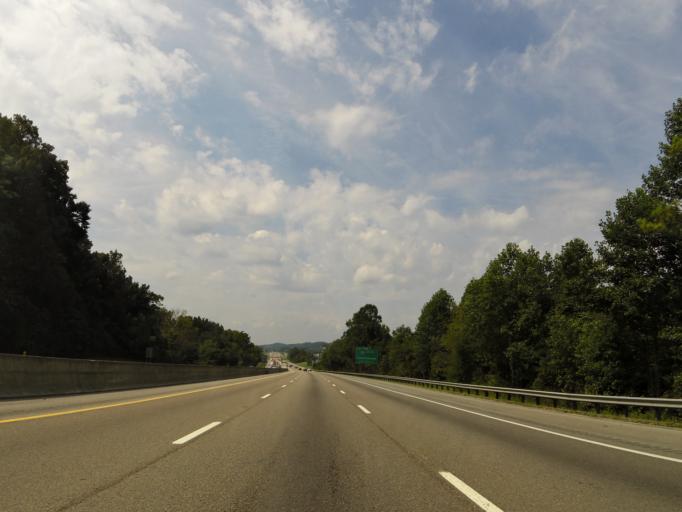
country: US
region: Tennessee
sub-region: Knox County
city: Farragut
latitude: 35.8860
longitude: -84.2210
